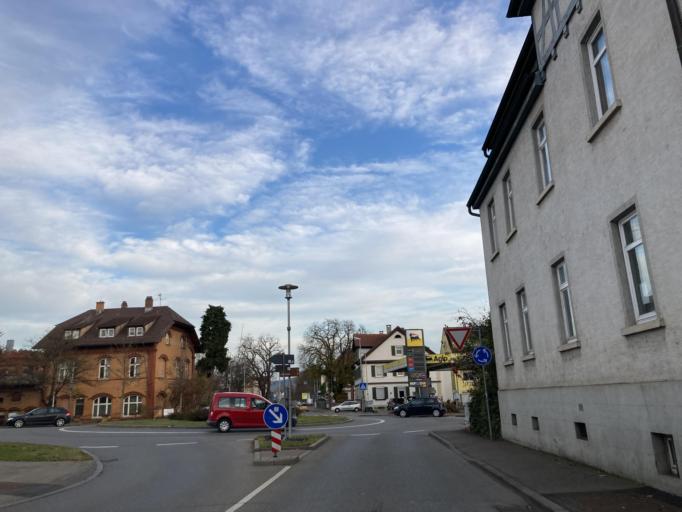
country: DE
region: Baden-Wuerttemberg
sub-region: Tuebingen Region
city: Rottenburg
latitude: 48.4735
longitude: 8.9379
